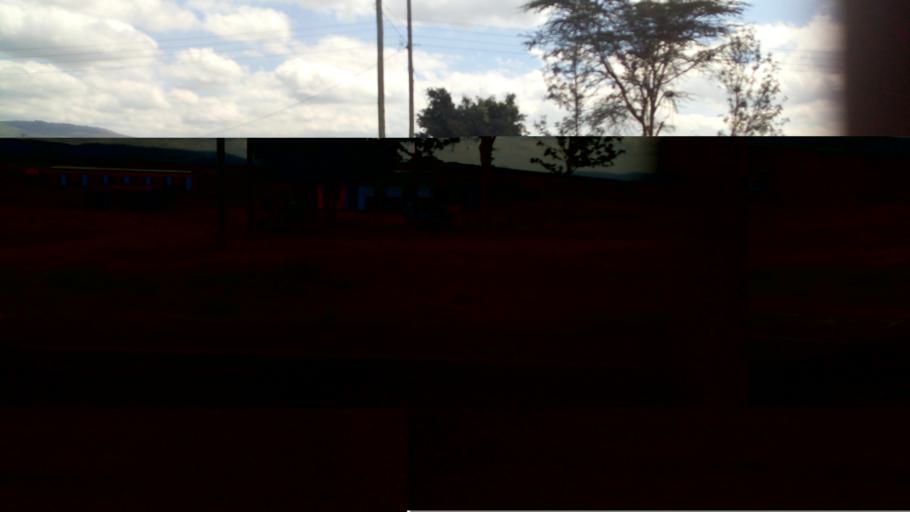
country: KE
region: Narok
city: Narok
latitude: -1.1071
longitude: 36.2381
